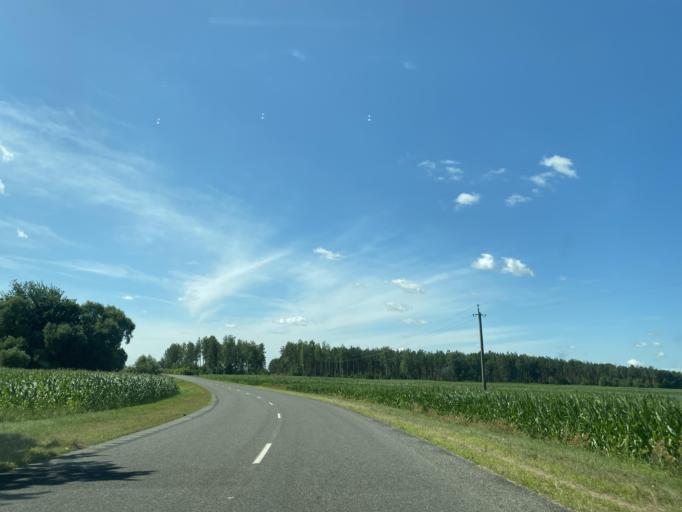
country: BY
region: Brest
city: Ivanava
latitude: 52.2219
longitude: 25.6318
